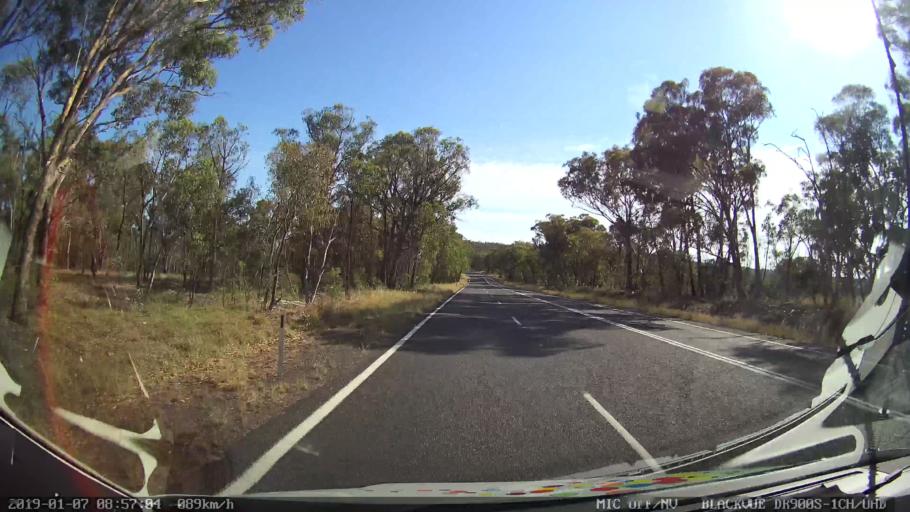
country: AU
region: New South Wales
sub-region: Tamworth Municipality
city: Kootingal
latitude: -30.7719
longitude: 151.3495
